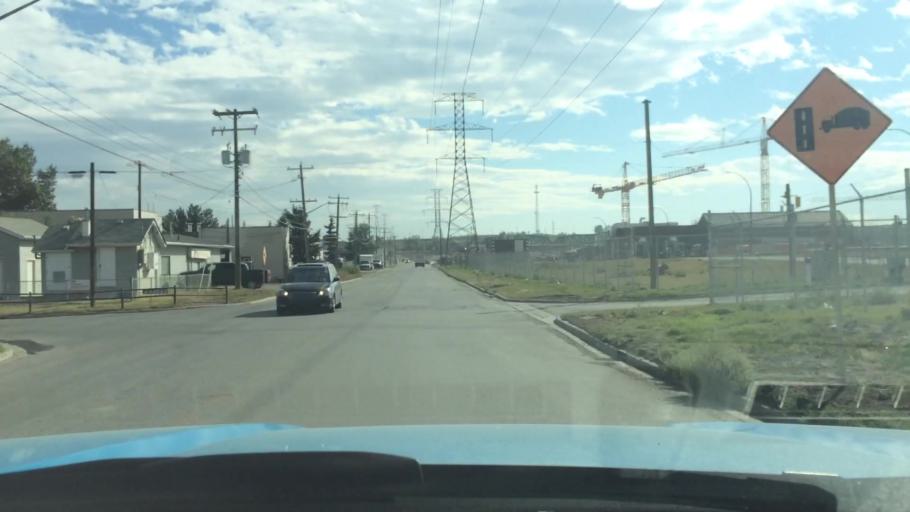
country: CA
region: Alberta
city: Calgary
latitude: 51.0155
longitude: -114.0211
